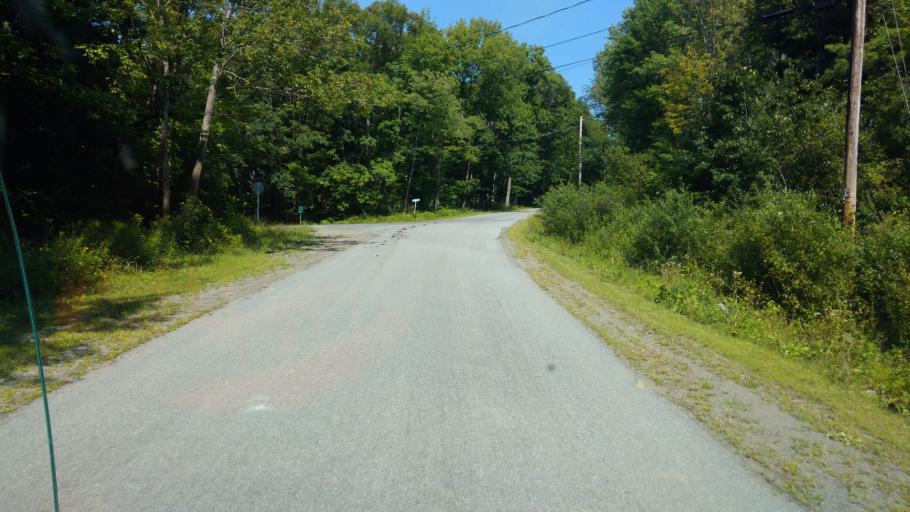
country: US
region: New York
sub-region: Allegany County
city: Belmont
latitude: 42.3268
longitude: -78.0739
